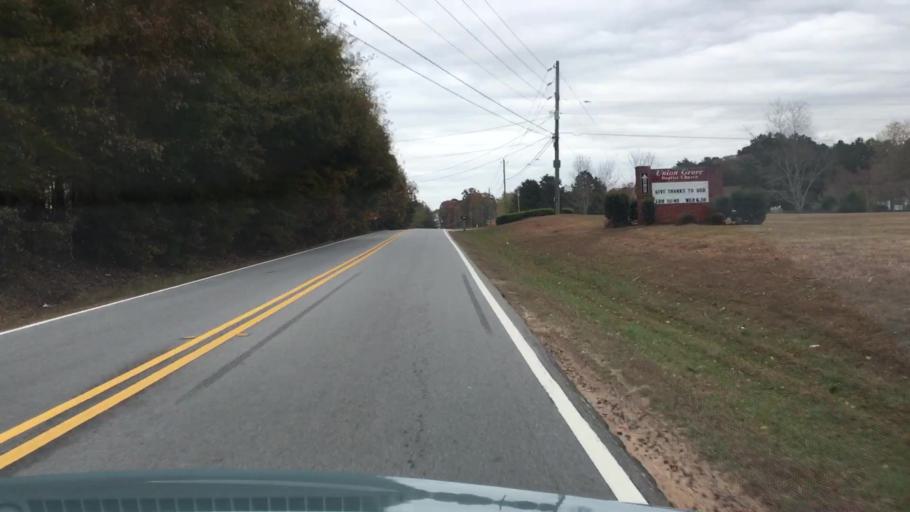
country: US
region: Georgia
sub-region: Henry County
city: McDonough
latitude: 33.5014
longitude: -84.0959
